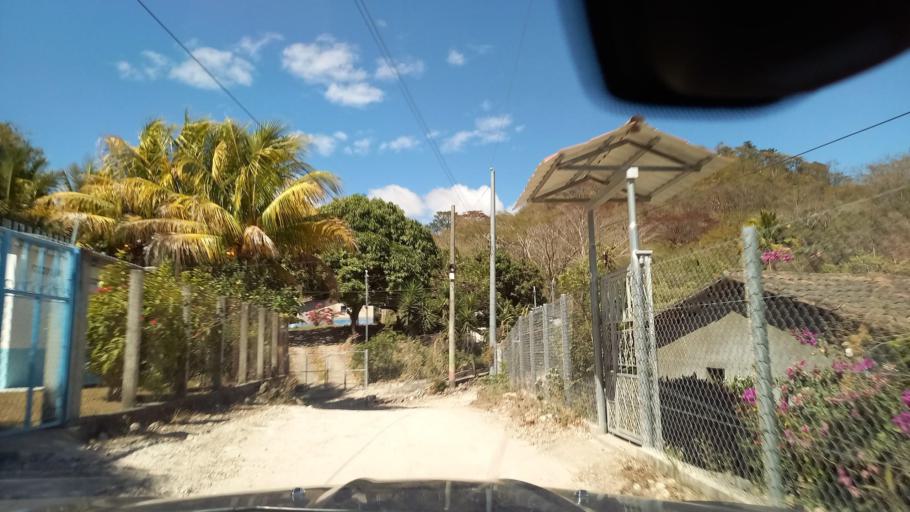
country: SV
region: Santa Ana
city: Metapan
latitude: 14.3739
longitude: -89.4935
